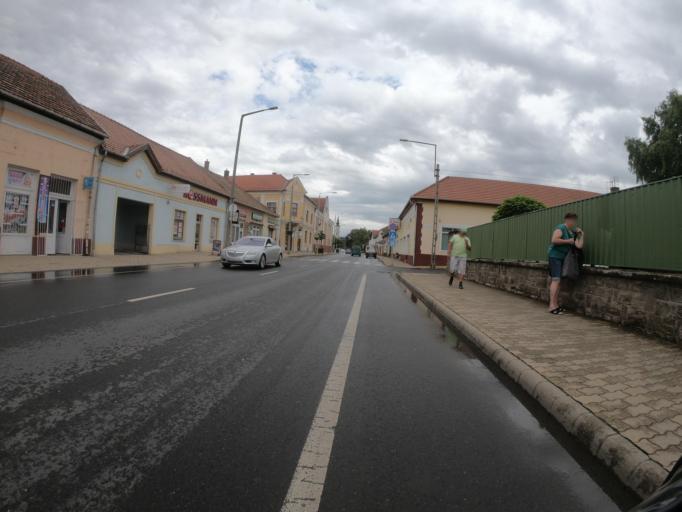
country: HU
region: Borsod-Abauj-Zemplen
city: Mezokovesd
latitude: 47.8090
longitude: 20.5693
